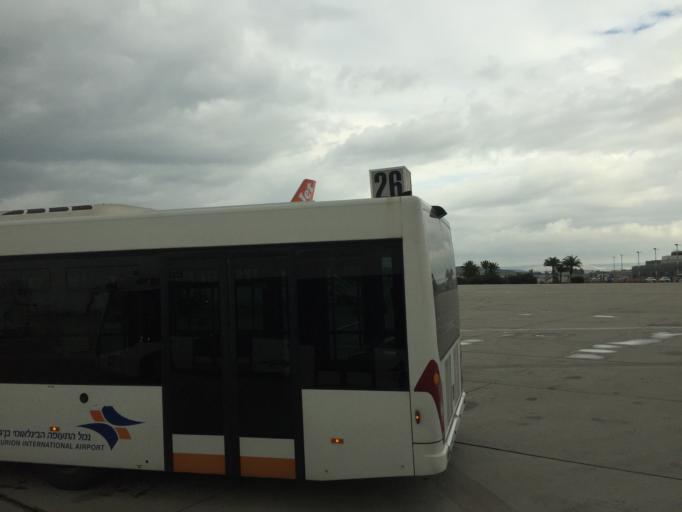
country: IL
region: Central District
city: Yehud
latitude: 31.9963
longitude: 34.8921
